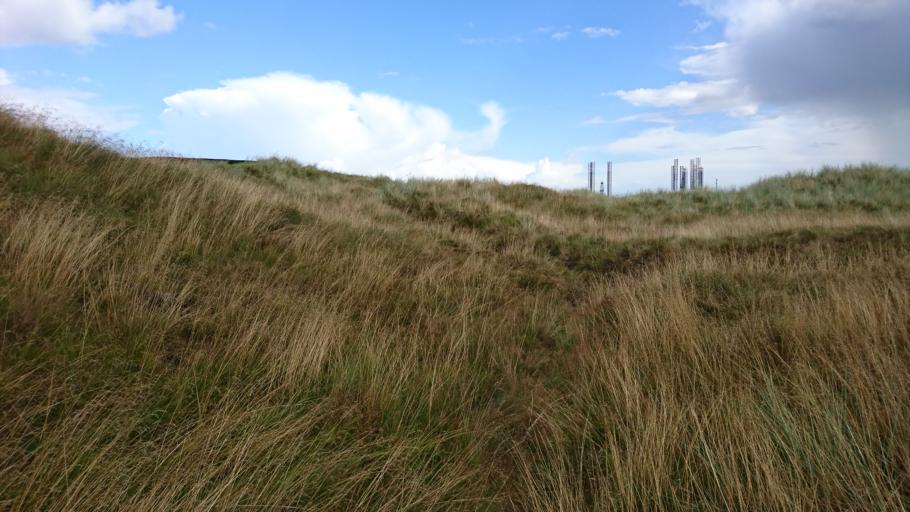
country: DK
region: South Denmark
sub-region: Fano Kommune
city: Nordby
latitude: 55.4610
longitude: 8.3966
